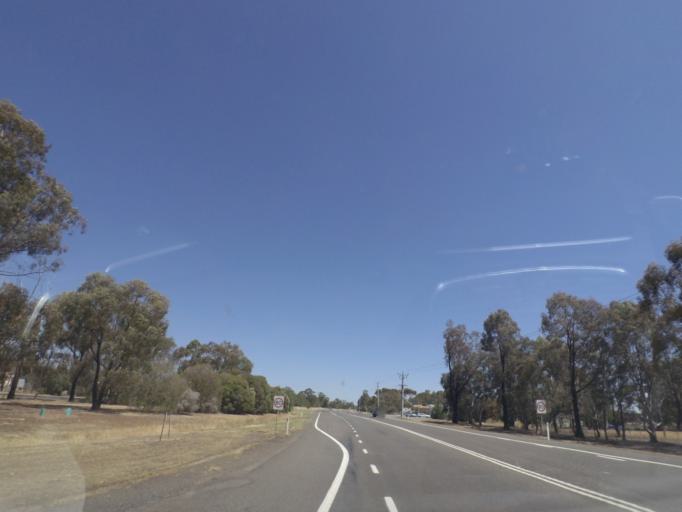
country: AU
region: Victoria
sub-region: Greater Shepparton
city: Shepparton
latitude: -36.2375
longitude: 145.4314
